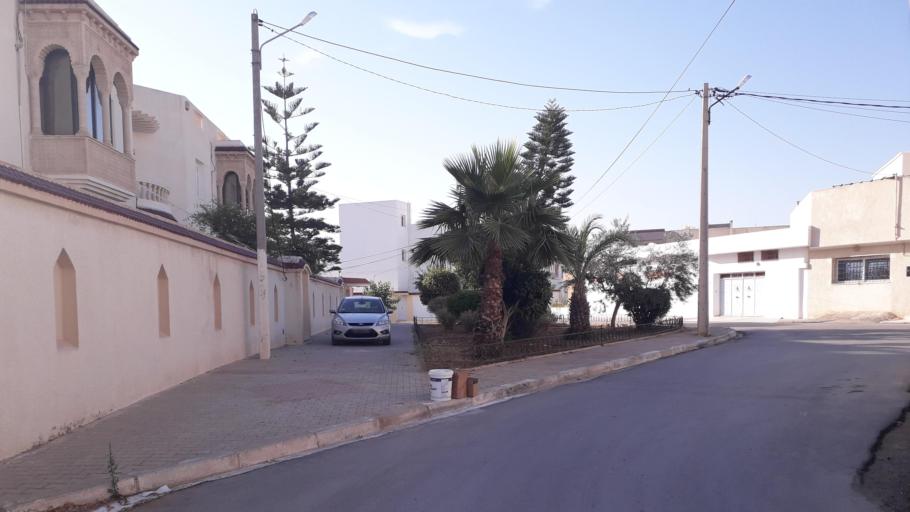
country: TN
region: Susah
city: Hammam Sousse
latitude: 35.8508
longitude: 10.5875
